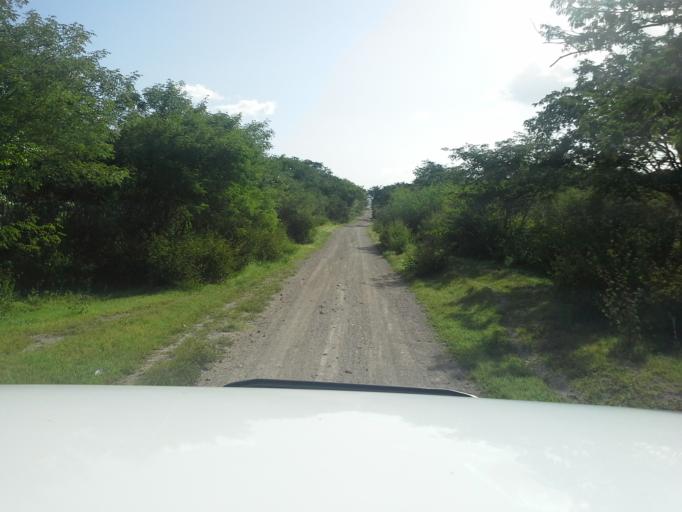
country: NI
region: Matagalpa
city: Ciudad Dario
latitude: 12.6626
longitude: -86.0638
